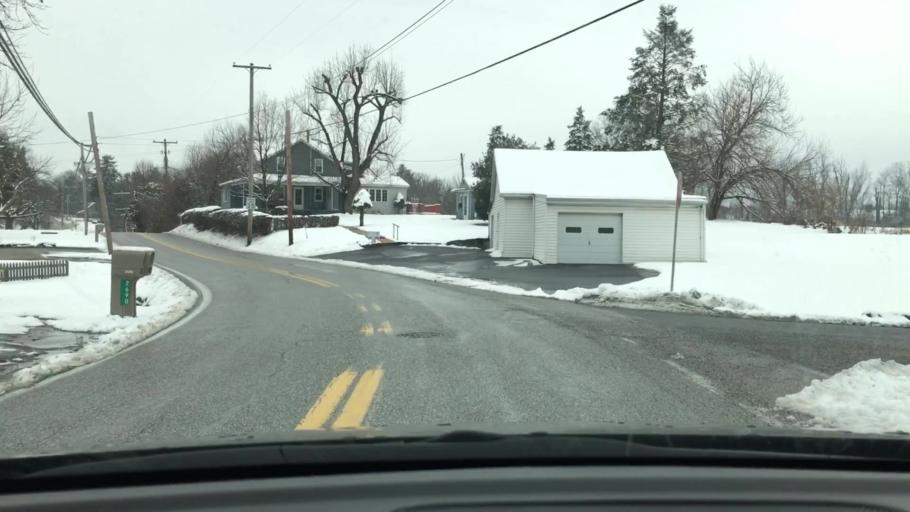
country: US
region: Pennsylvania
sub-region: York County
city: Emigsville
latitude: 40.0068
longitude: -76.7513
